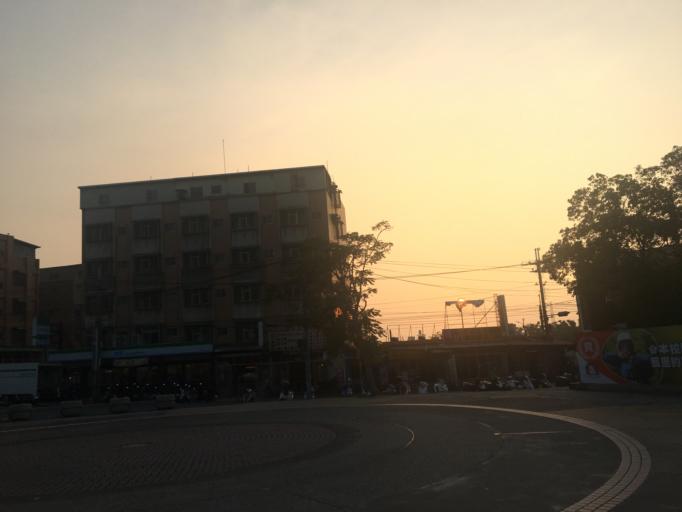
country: TW
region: Taiwan
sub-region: Hsinchu
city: Hsinchu
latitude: 24.7573
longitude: 120.9526
